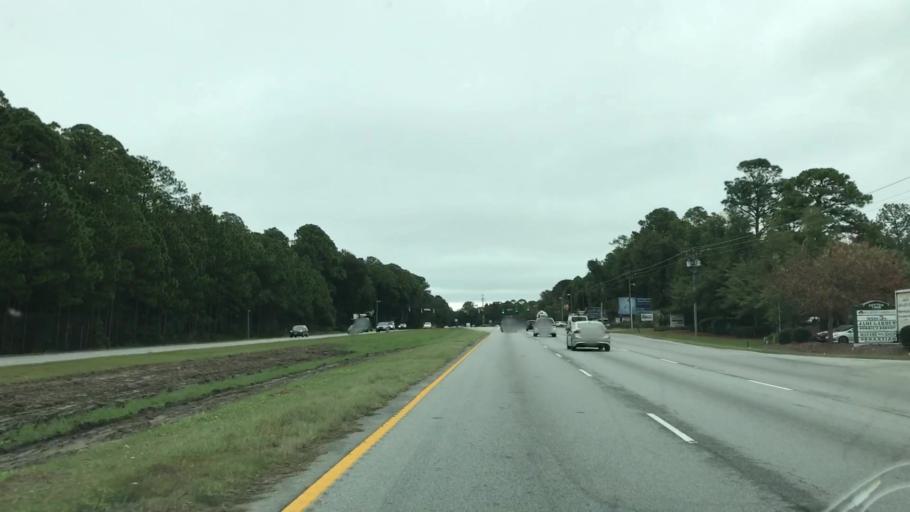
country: US
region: South Carolina
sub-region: Beaufort County
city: Bluffton
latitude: 32.2454
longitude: -80.8285
